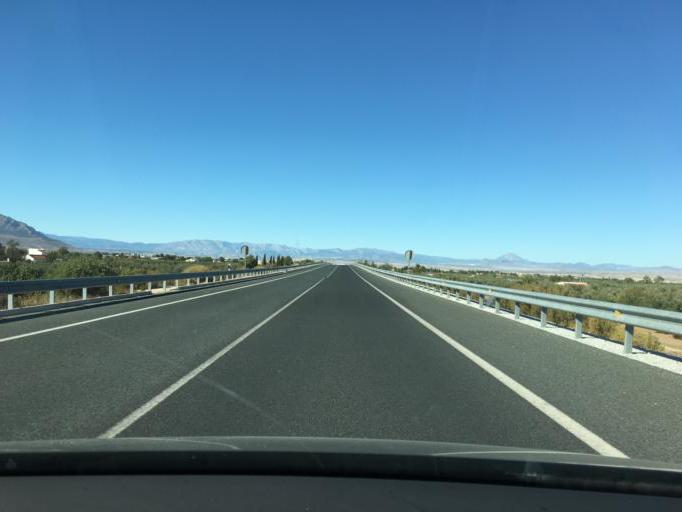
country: ES
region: Andalusia
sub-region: Provincia de Granada
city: Baza
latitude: 37.4882
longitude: -2.7399
